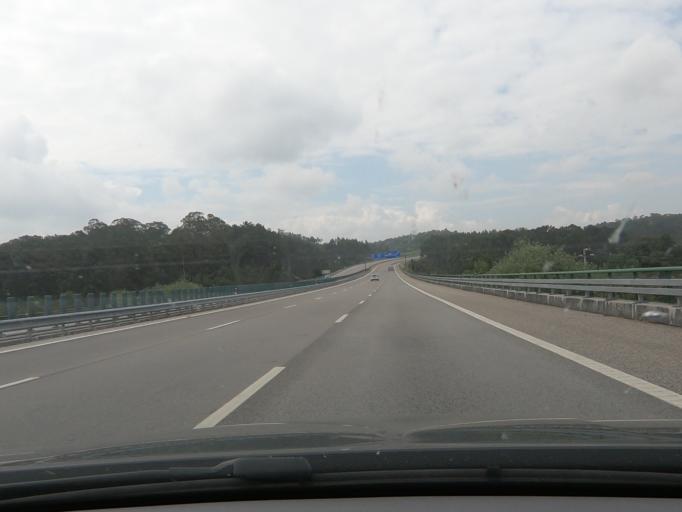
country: PT
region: Leiria
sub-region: Leiria
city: Souto da Carpalhosa
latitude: 39.8670
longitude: -8.8249
